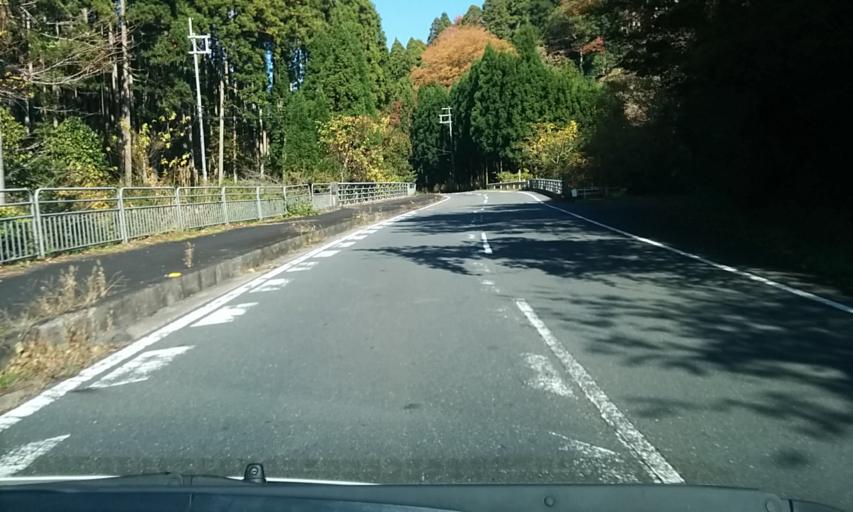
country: JP
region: Kyoto
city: Kameoka
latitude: 35.1559
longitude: 135.5134
